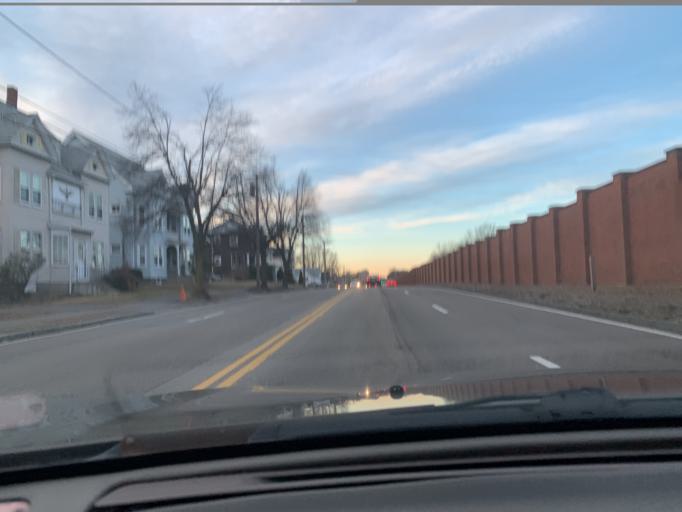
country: US
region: Massachusetts
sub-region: Norfolk County
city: Quincy
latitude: 42.2676
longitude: -71.0218
